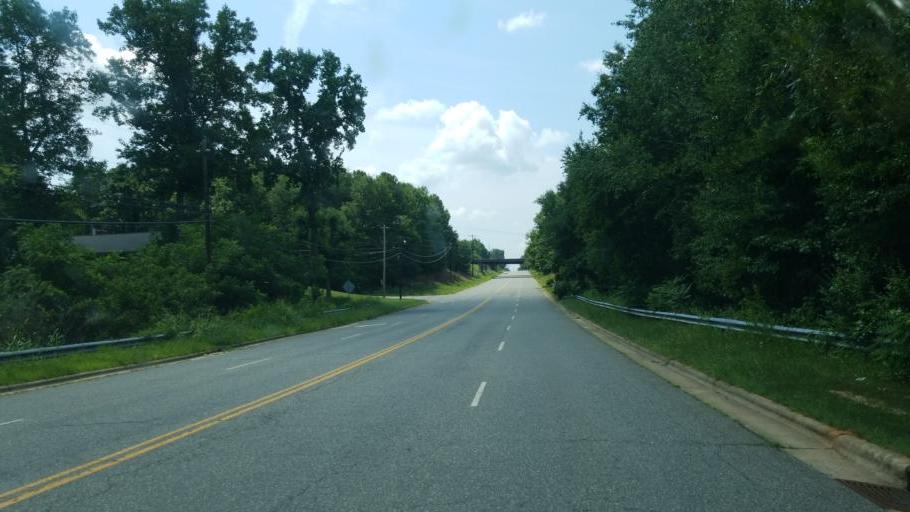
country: US
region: North Carolina
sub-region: Cleveland County
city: Kings Mountain
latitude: 35.2550
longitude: -81.3465
